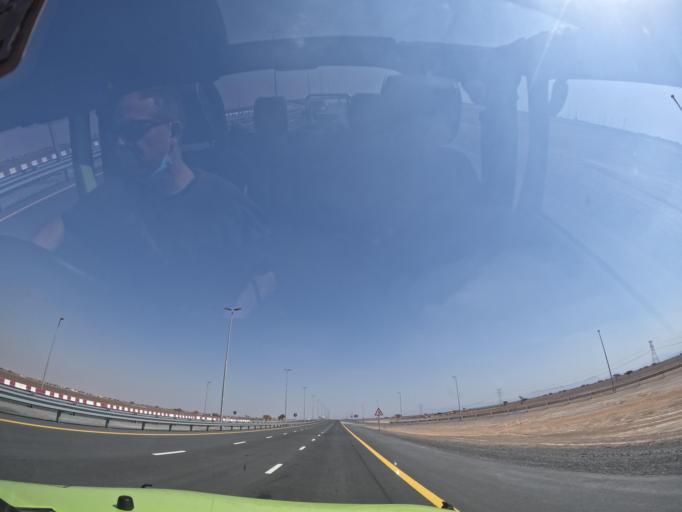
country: AE
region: Ash Shariqah
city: Adh Dhayd
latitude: 24.9328
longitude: 55.8182
